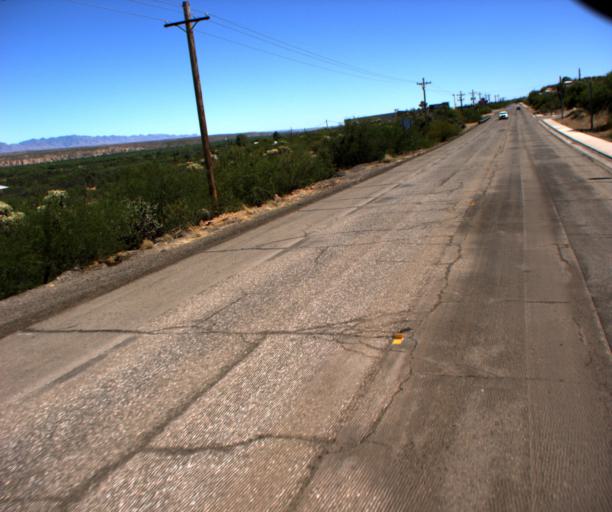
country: US
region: Arizona
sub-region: Pinal County
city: Mammoth
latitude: 32.7278
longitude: -110.6464
